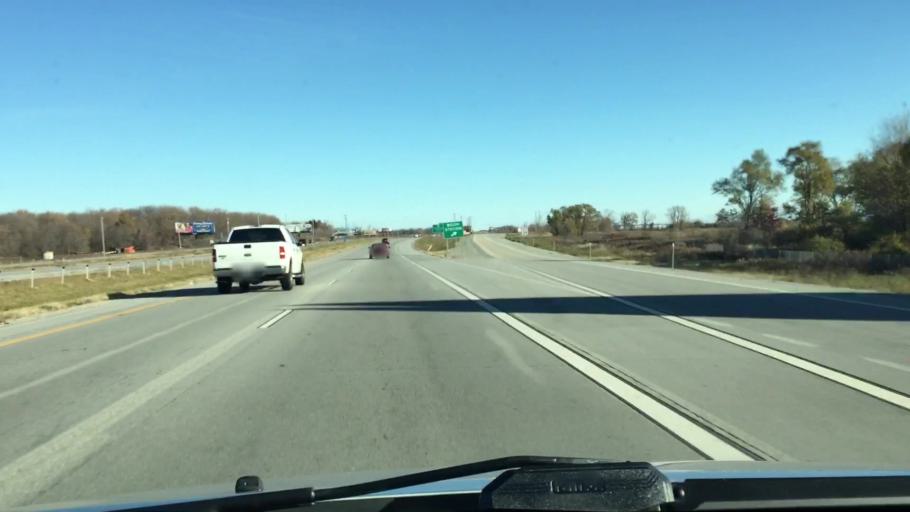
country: US
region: Wisconsin
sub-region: Brown County
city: Wrightstown
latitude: 44.3371
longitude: -88.2036
